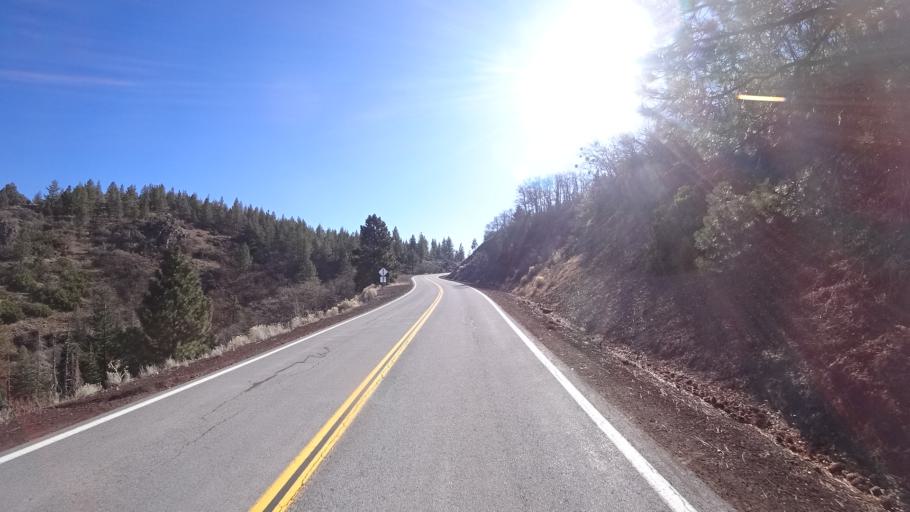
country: US
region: California
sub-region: Siskiyou County
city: Weed
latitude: 41.4389
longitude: -122.6404
